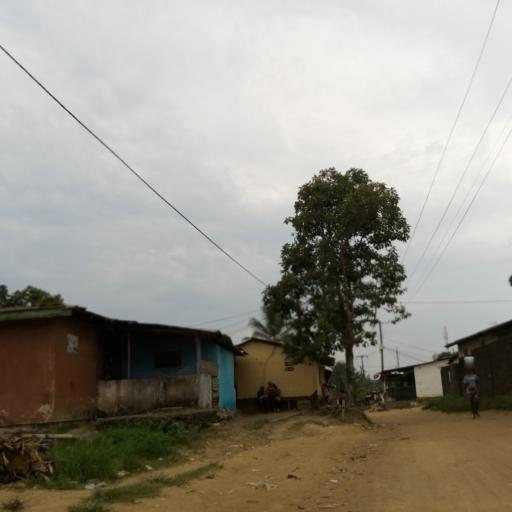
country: LR
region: Montserrado
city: Monrovia
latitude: 6.2956
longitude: -10.6814
